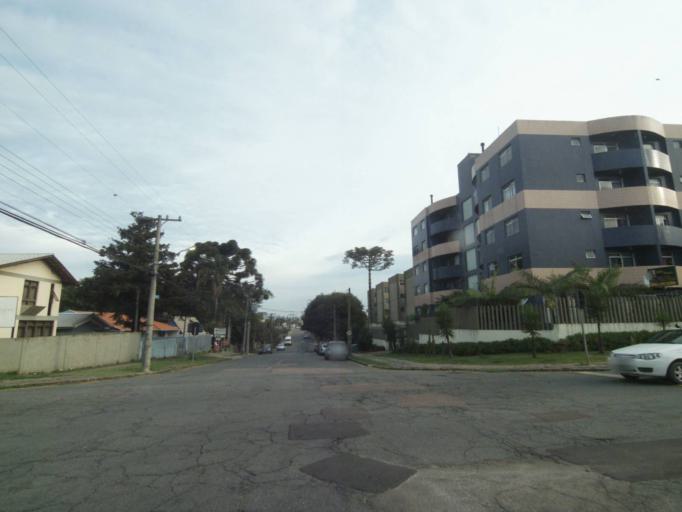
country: BR
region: Parana
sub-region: Curitiba
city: Curitiba
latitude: -25.4320
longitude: -49.2358
